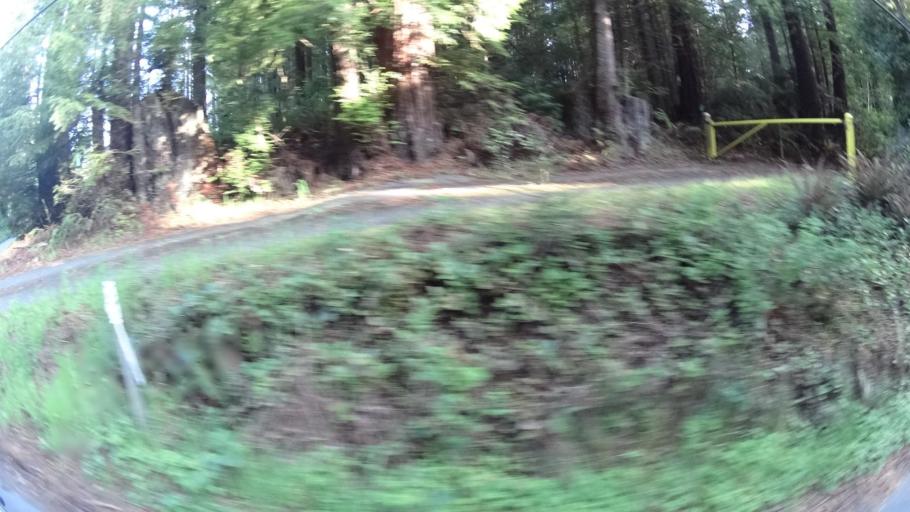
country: US
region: California
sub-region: Humboldt County
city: Myrtletown
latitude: 40.7721
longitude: -124.1164
